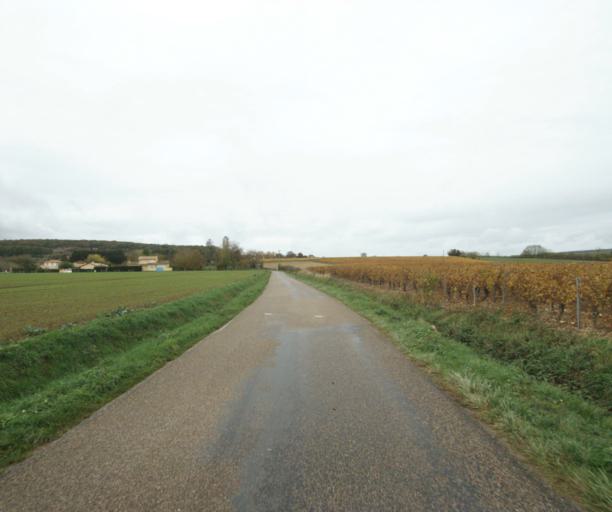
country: FR
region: Bourgogne
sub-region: Departement de Saone-et-Loire
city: Saint-Martin-Belle-Roche
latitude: 46.4697
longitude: 4.8567
